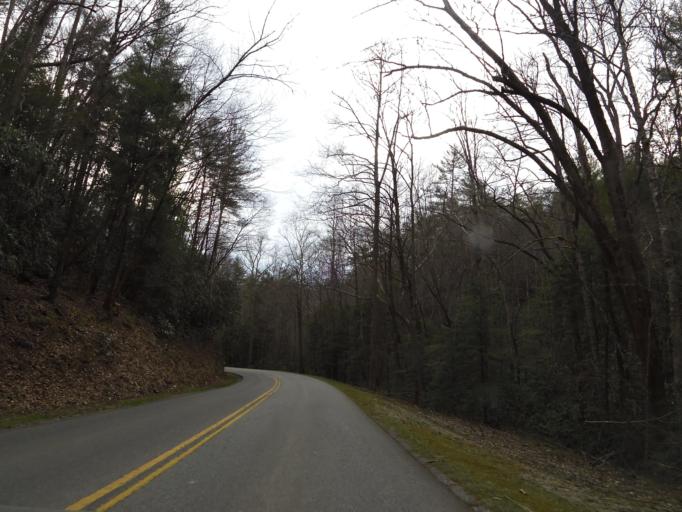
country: US
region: Tennessee
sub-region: Blount County
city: Wildwood
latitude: 35.6183
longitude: -83.7357
